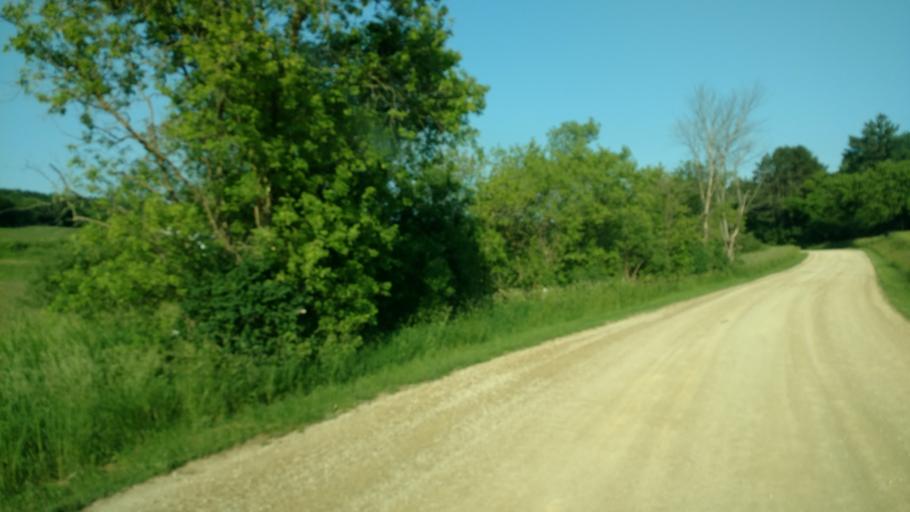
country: US
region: Wisconsin
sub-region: Vernon County
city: Hillsboro
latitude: 43.6316
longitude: -90.3488
